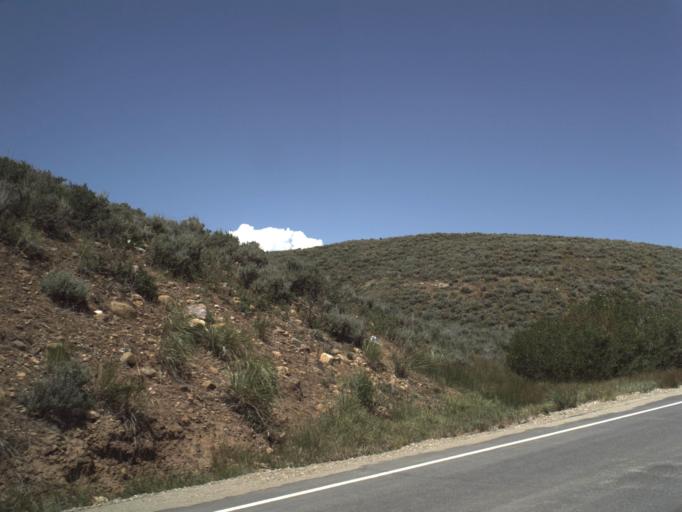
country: US
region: Utah
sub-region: Weber County
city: Wolf Creek
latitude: 41.4043
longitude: -111.5990
